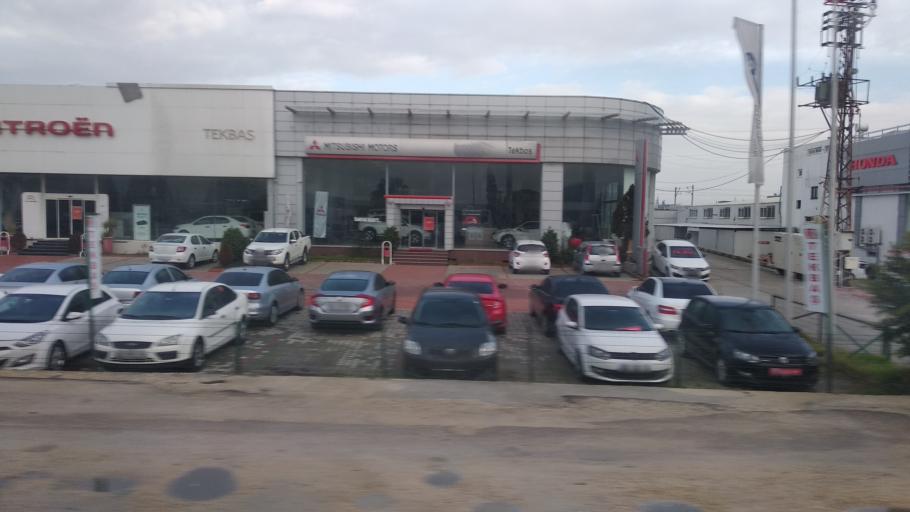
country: TR
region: Adana
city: Seyhan
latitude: 36.9951
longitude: 35.2161
